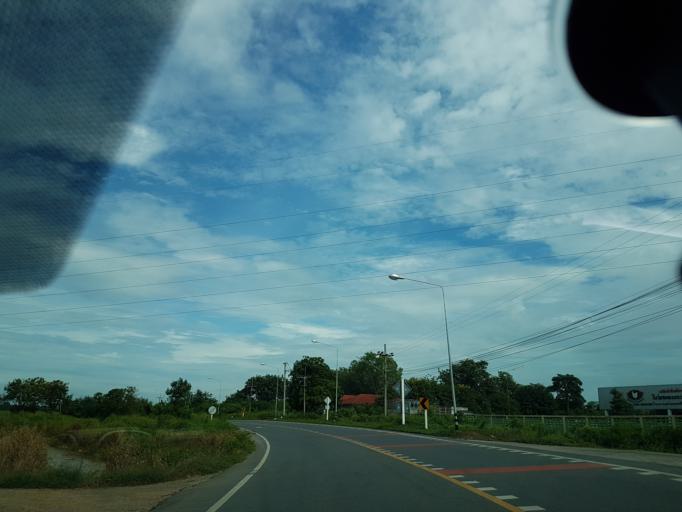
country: TH
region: Ang Thong
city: Chaiyo
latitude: 14.7224
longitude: 100.4934
